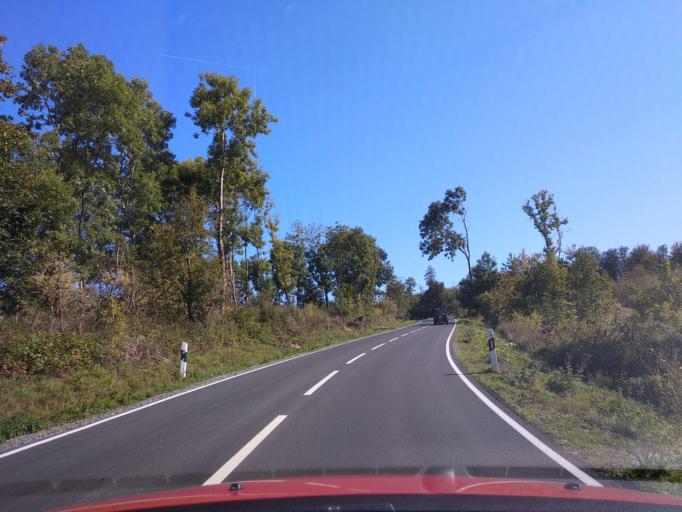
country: DE
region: Lower Saxony
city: Boffzen
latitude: 51.7325
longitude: 9.2901
